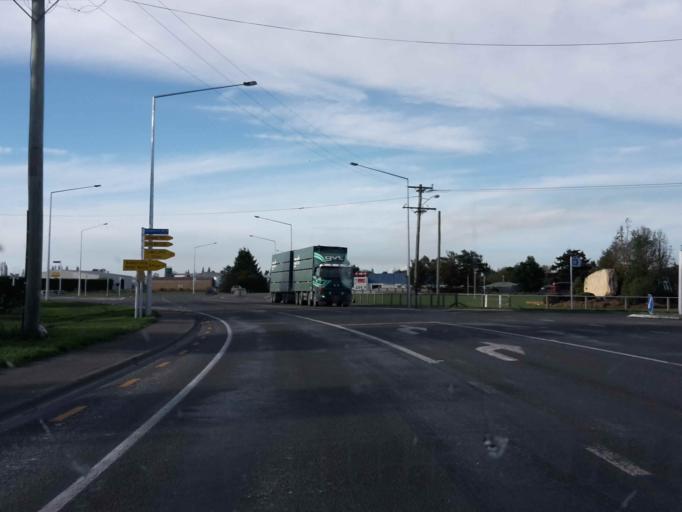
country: NZ
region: Canterbury
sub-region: Ashburton District
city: Tinwald
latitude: -44.0025
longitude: 171.5695
